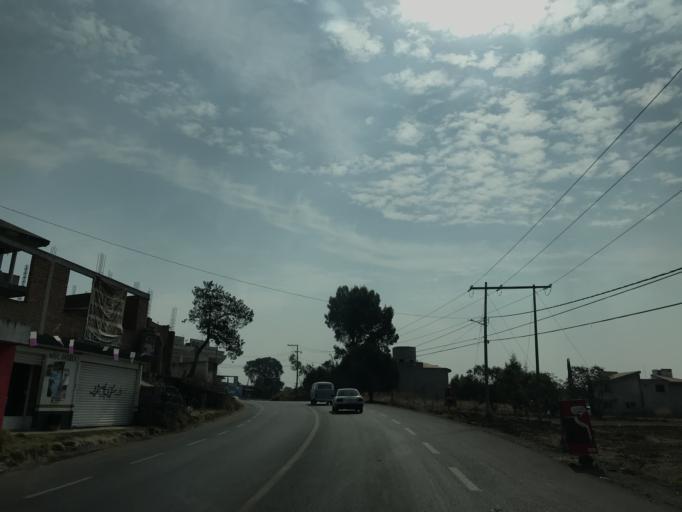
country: MX
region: Tlaxcala
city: Tenancingo
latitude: 19.1518
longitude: -98.2098
